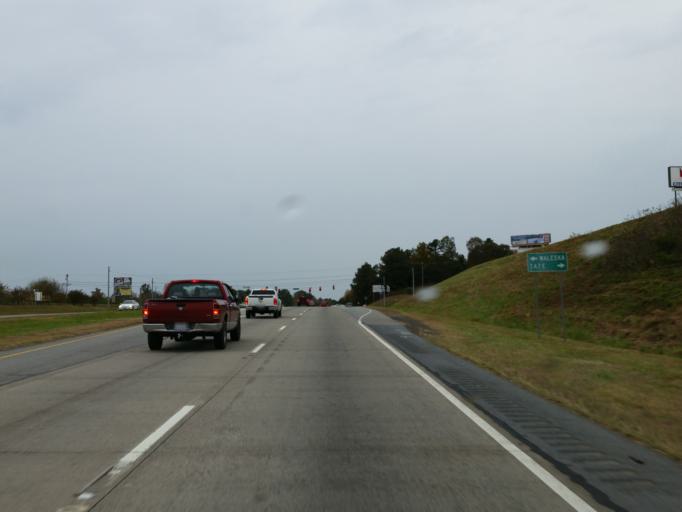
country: US
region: Georgia
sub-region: Pickens County
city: Nelson
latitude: 34.4054
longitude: -84.4205
